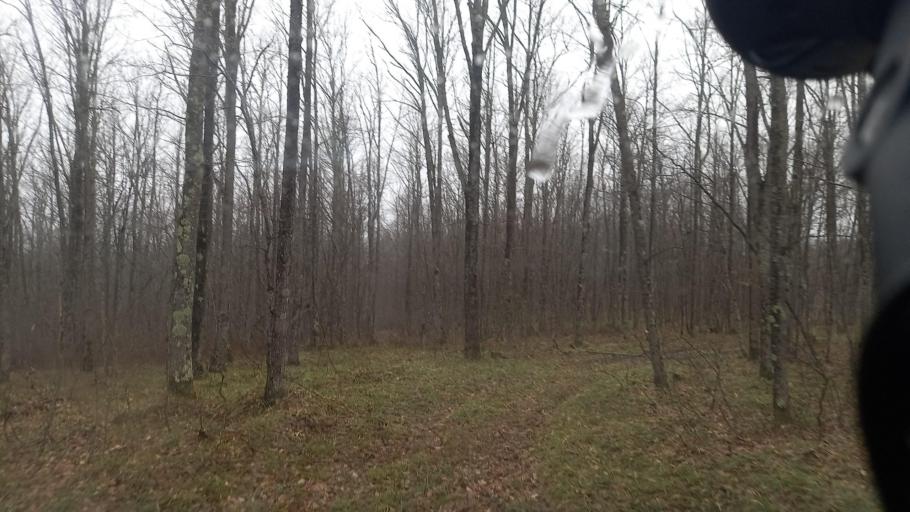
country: RU
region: Krasnodarskiy
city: Saratovskaya
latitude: 44.6199
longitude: 39.2542
